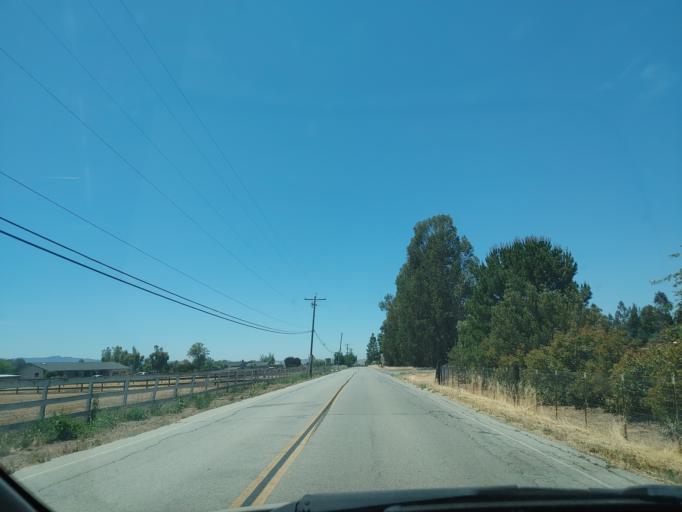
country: US
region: California
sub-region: San Benito County
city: Hollister
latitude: 36.9155
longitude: -121.3553
